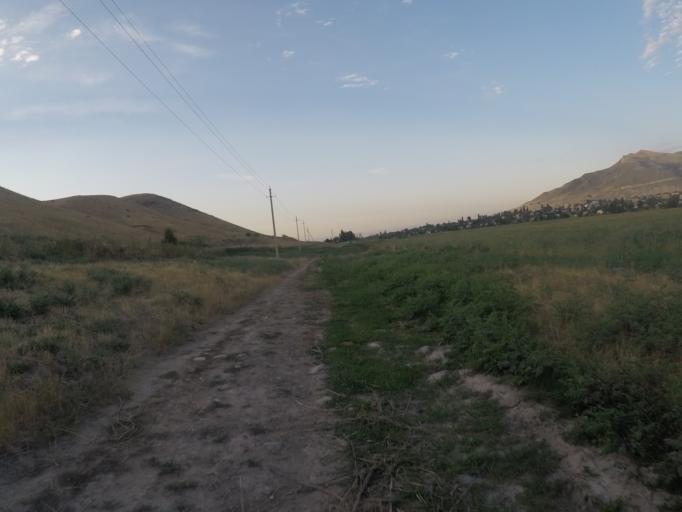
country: KG
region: Chuy
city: Bishkek
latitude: 42.7606
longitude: 74.6363
